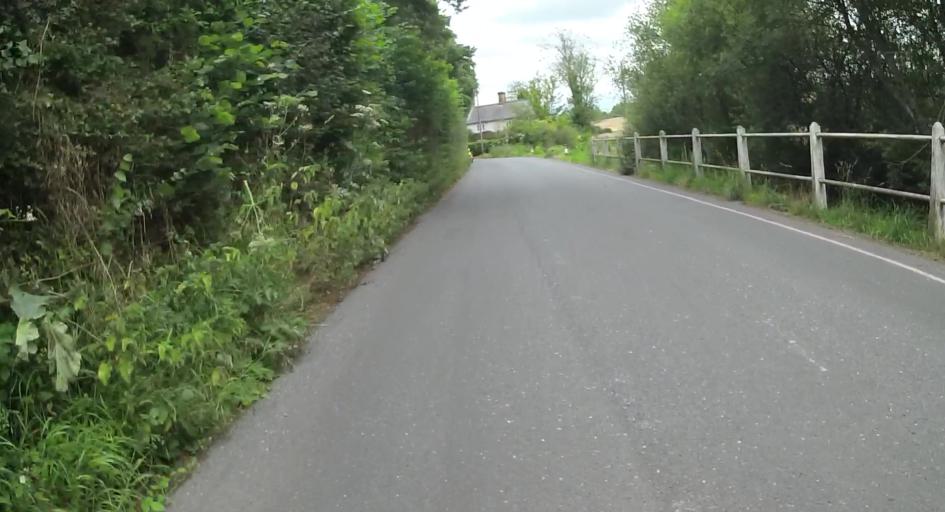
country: GB
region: England
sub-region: Hampshire
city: Swanmore
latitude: 51.0513
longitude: -1.1679
